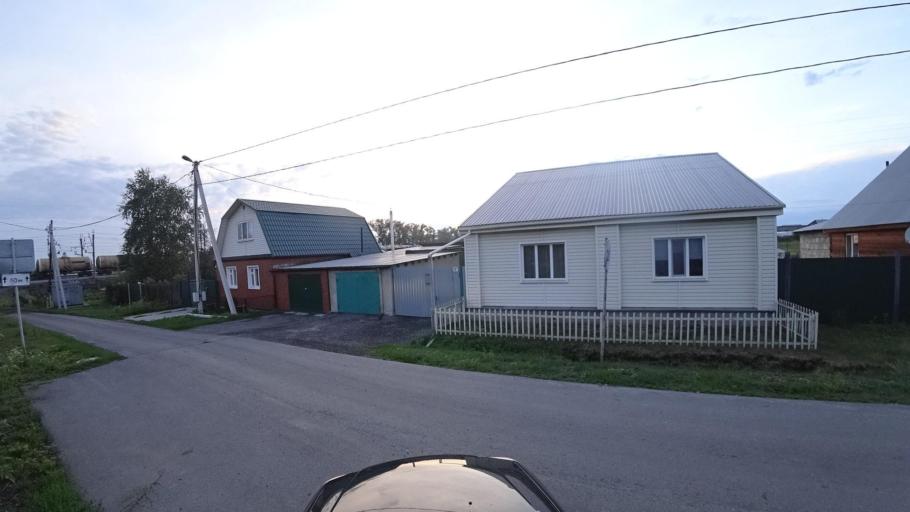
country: RU
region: Sverdlovsk
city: Kamyshlov
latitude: 56.8550
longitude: 62.6959
